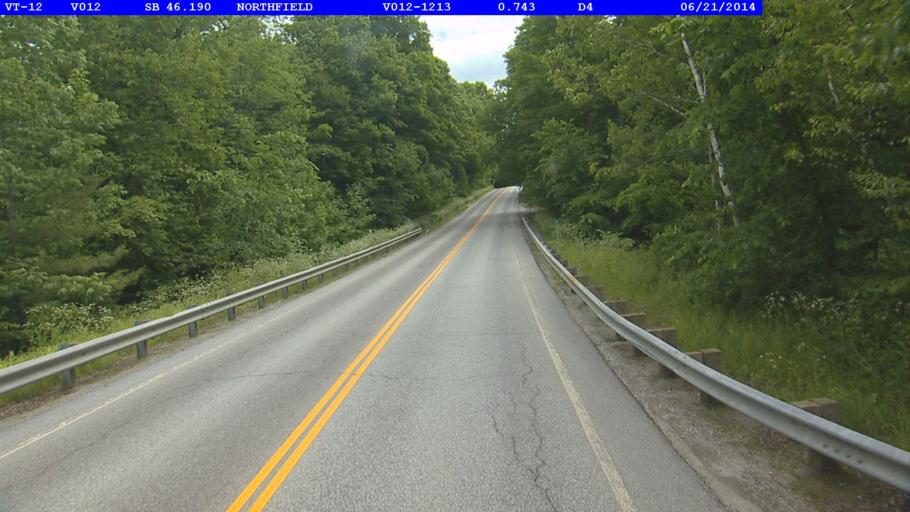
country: US
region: Vermont
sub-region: Washington County
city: Northfield
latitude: 44.1031
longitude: -72.6433
